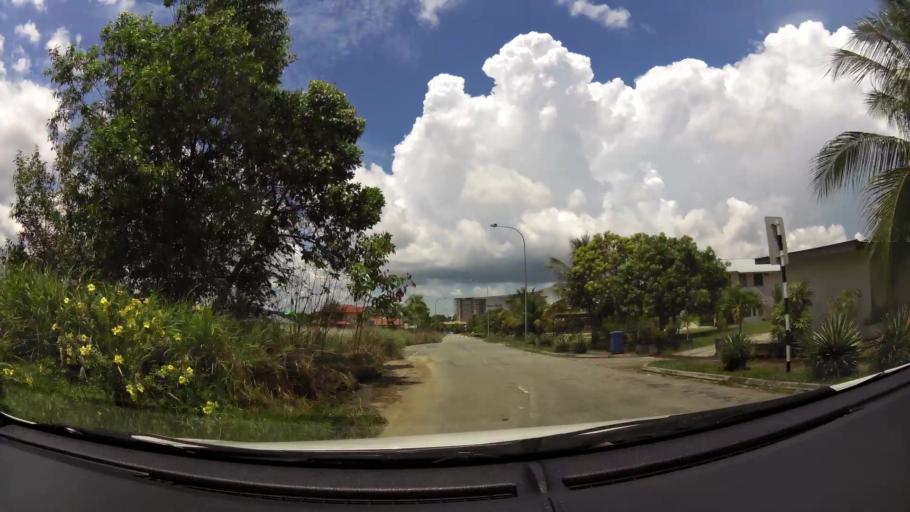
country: BN
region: Brunei and Muara
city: Bandar Seri Begawan
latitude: 4.9603
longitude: 114.9133
